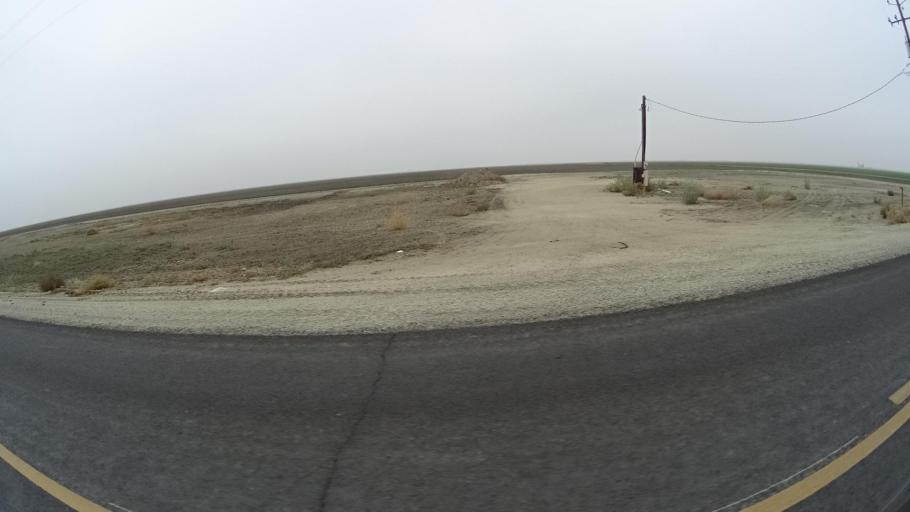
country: US
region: California
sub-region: Kern County
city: Rosedale
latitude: 35.1804
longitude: -119.1919
